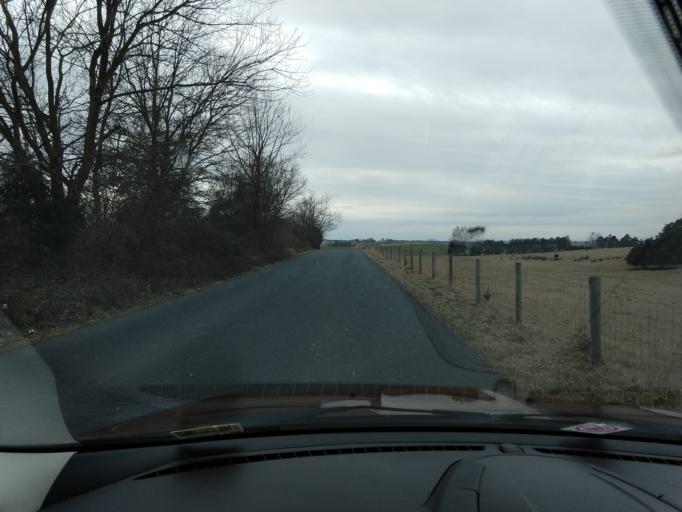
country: US
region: Virginia
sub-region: Rockingham County
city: Grottoes
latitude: 38.2332
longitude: -78.8771
